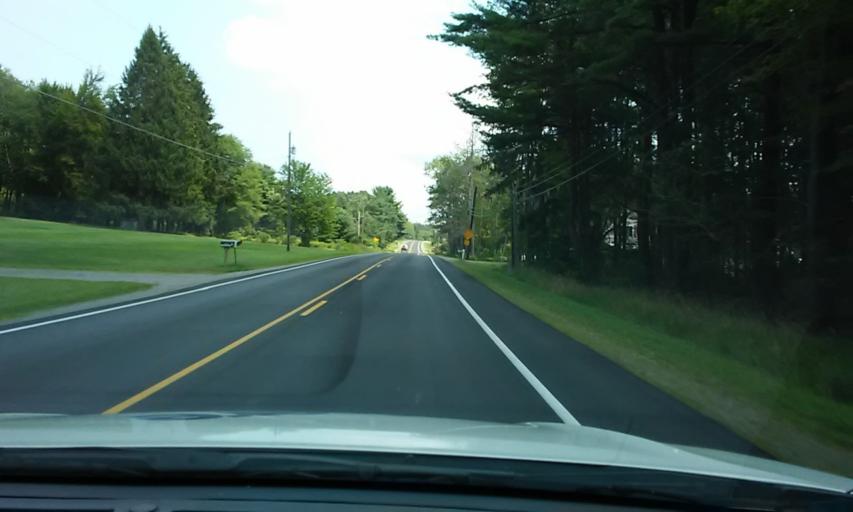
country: US
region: Pennsylvania
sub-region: Elk County
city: Saint Marys
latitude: 41.4484
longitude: -78.4638
